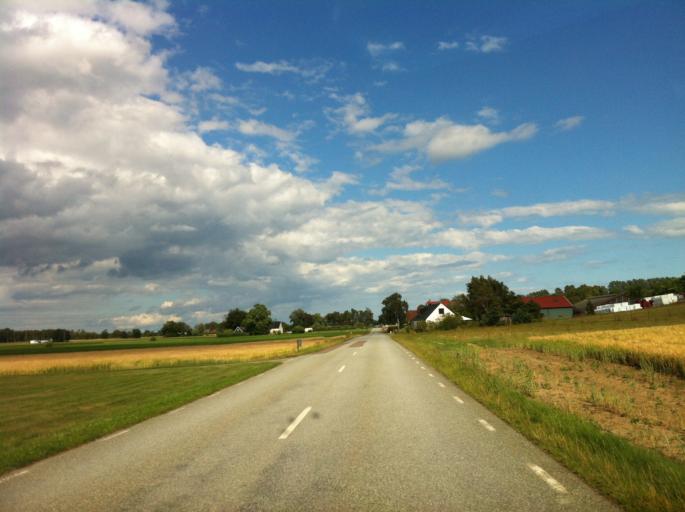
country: SE
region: Skane
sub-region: Ystads Kommun
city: Kopingebro
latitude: 55.3999
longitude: 14.0282
